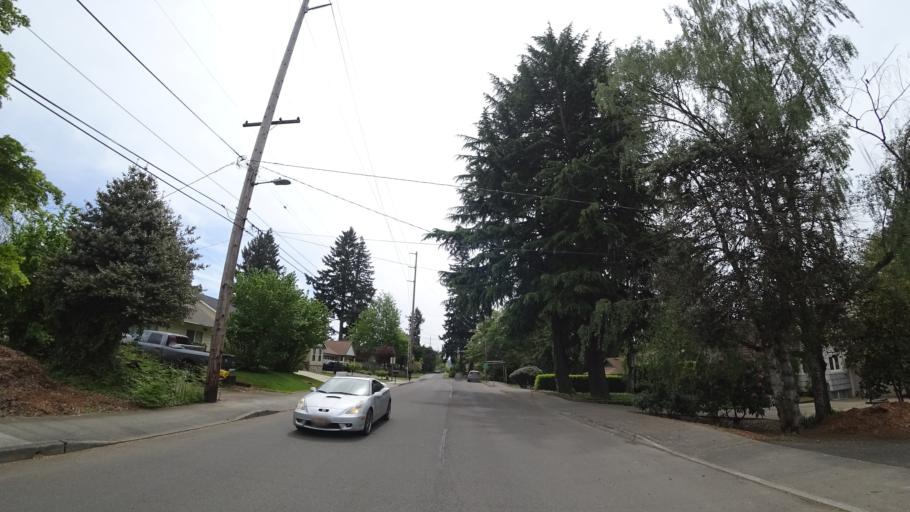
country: US
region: Oregon
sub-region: Clackamas County
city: Milwaukie
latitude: 45.4489
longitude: -122.6222
